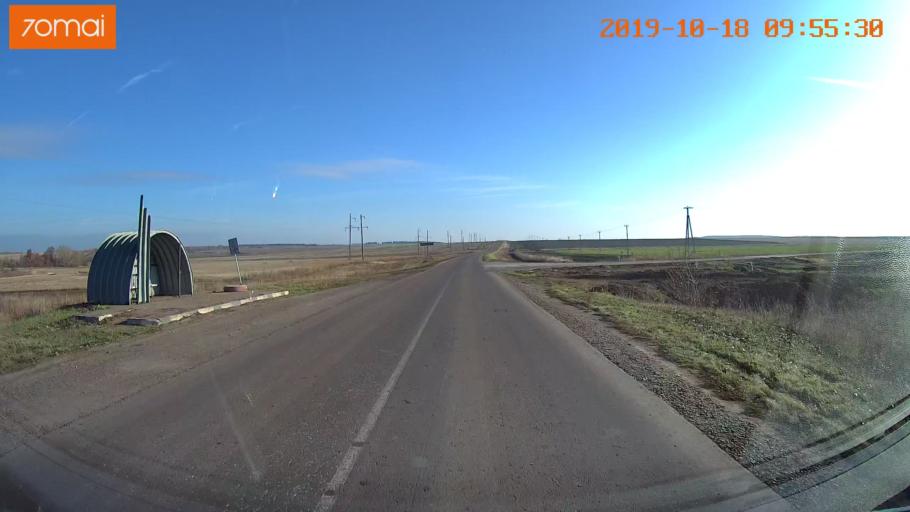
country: RU
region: Tula
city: Kazachka
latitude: 53.3707
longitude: 38.3662
